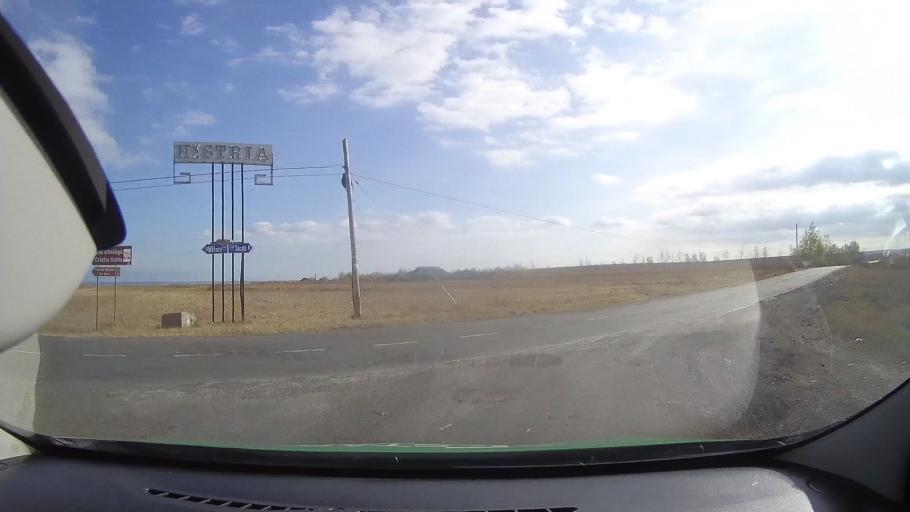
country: RO
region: Constanta
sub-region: Comuna Istria
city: Nuntasi
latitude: 44.5288
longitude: 28.6840
